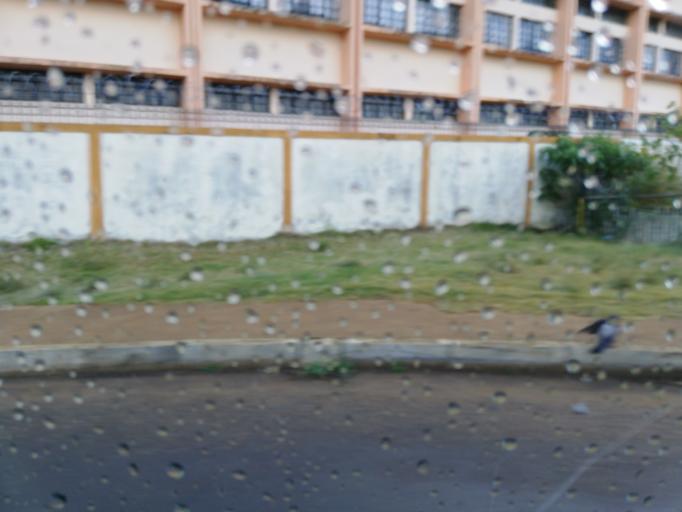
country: MU
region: Plaines Wilhems
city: Ebene
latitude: -20.2409
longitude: 57.4831
